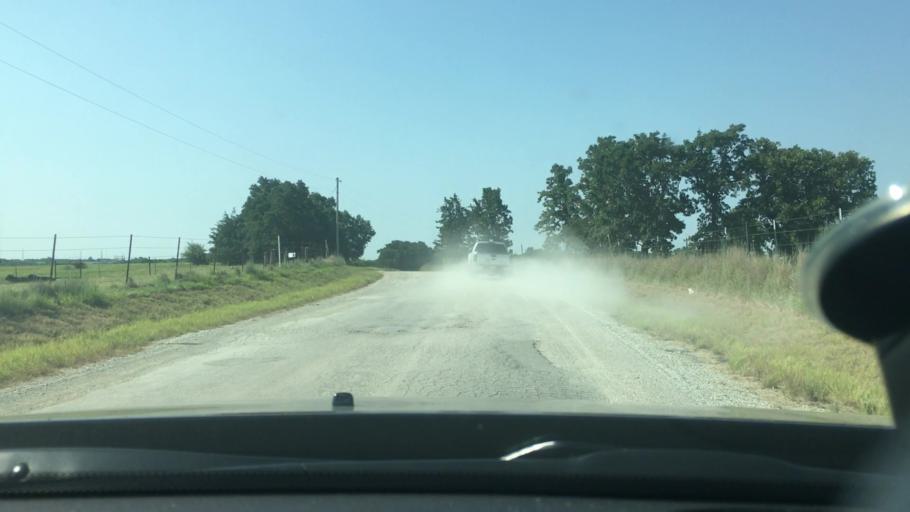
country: US
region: Oklahoma
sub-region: Garvin County
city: Lindsay
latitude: 34.7725
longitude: -97.6122
